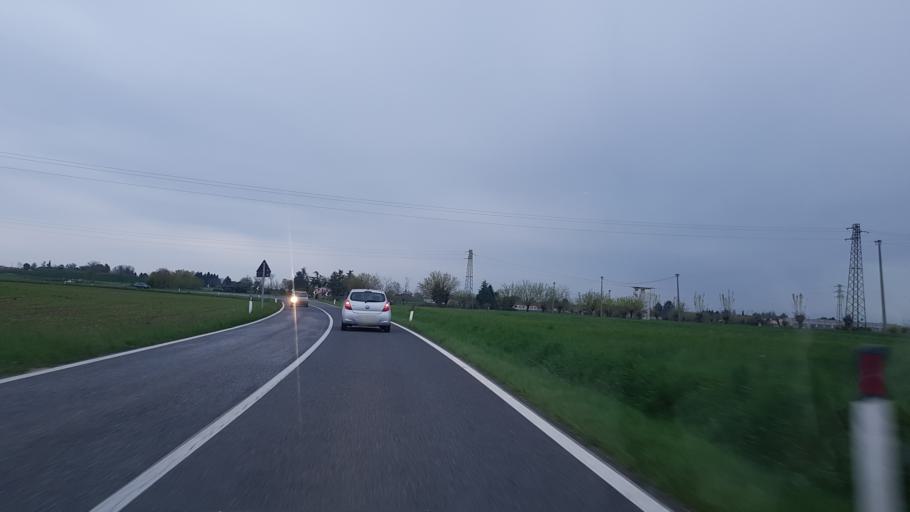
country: IT
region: Friuli Venezia Giulia
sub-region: Provincia di Udine
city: Sottoselva
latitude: 45.9013
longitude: 13.3228
